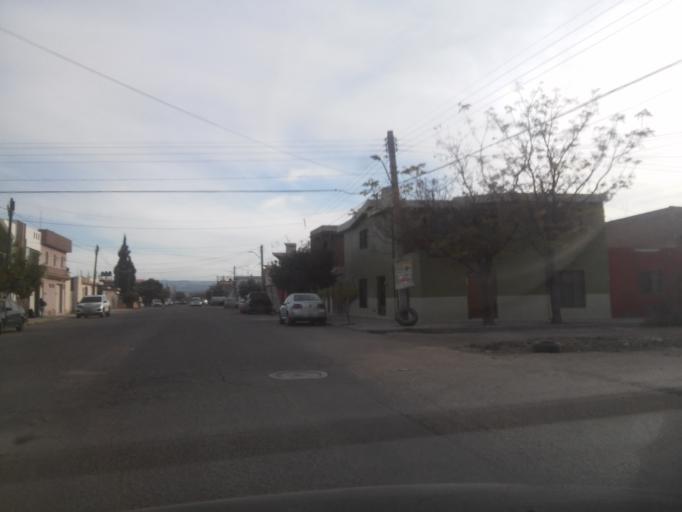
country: MX
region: Durango
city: Victoria de Durango
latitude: 24.0222
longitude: -104.6350
